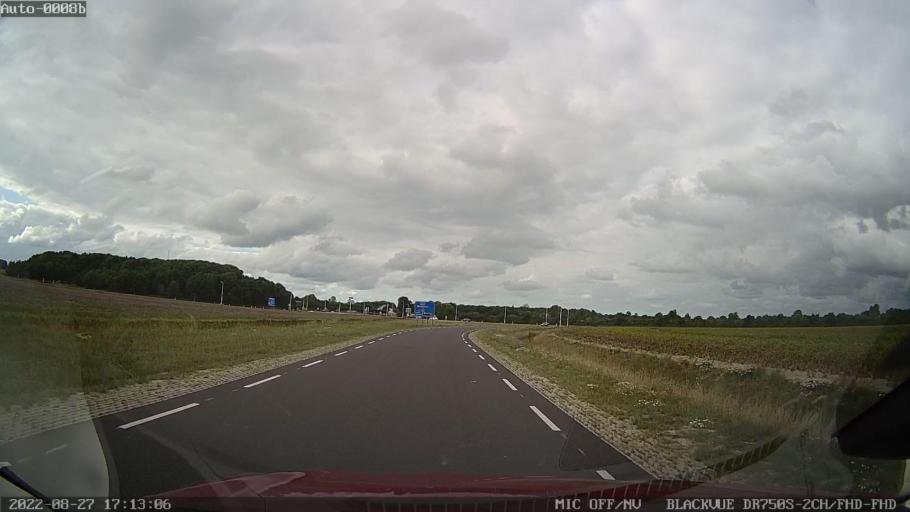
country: NL
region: Zeeland
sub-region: Schouwen-Duiveland
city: Scharendijke
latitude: 51.7321
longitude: 3.8302
